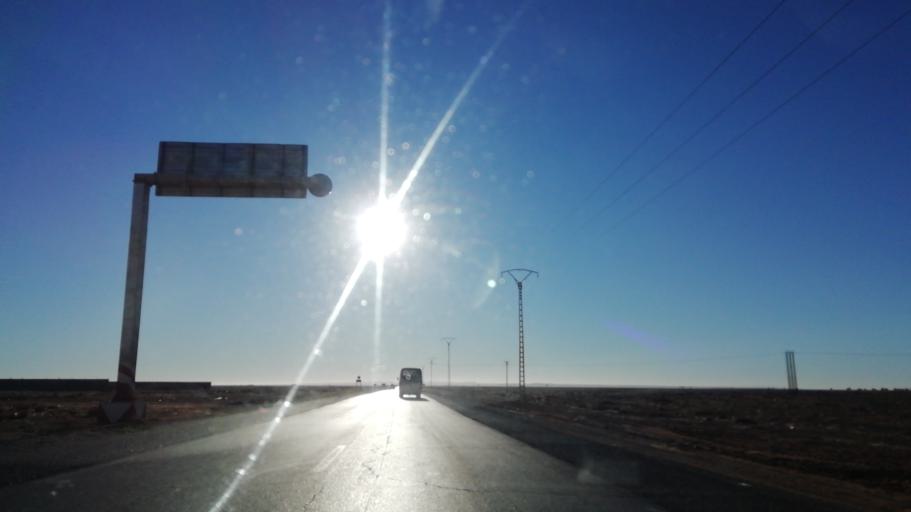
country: DZ
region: Saida
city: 'Ain el Hadjar
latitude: 34.0204
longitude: 0.1046
